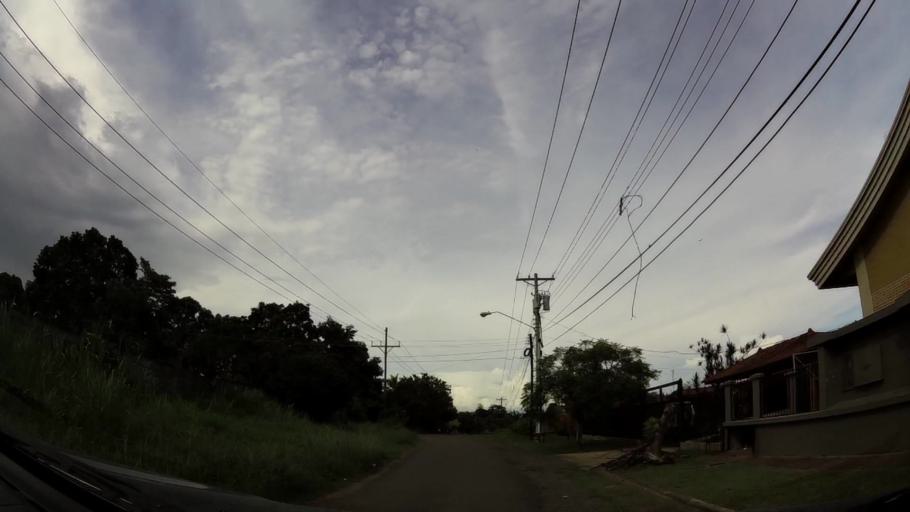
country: PA
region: Panama
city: Guadalupe
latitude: 8.8633
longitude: -79.8081
